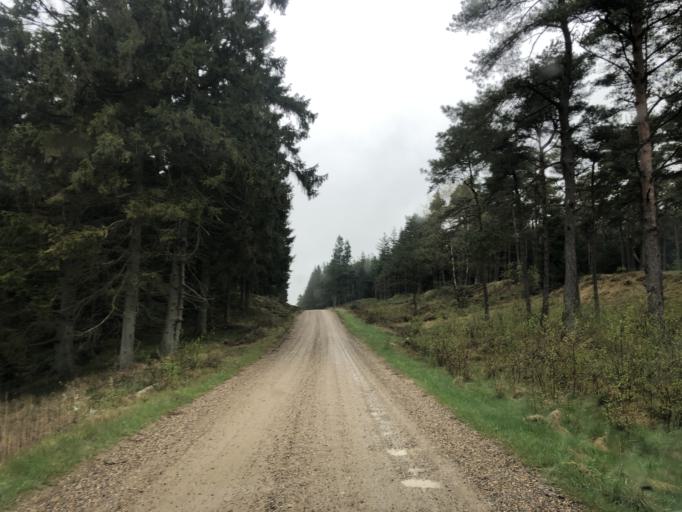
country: DK
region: Central Jutland
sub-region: Lemvig Kommune
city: Lemvig
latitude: 56.4785
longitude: 8.3718
